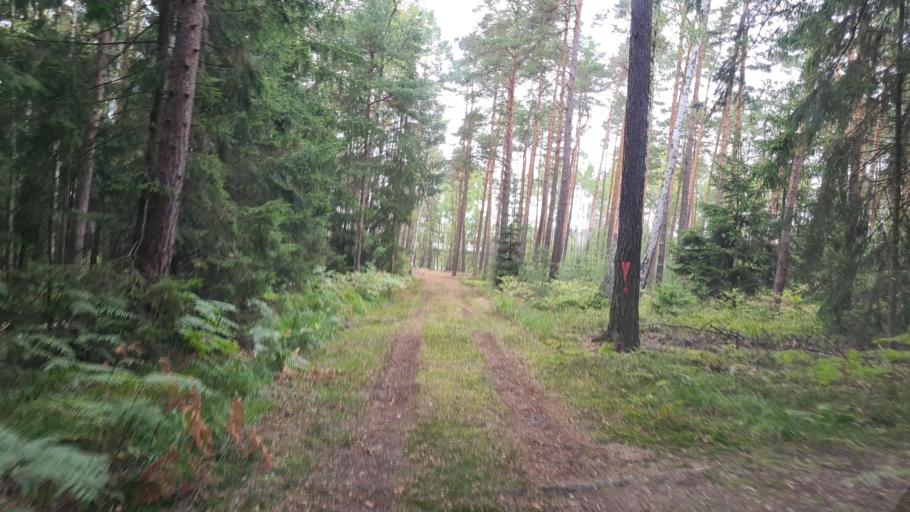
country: DE
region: Brandenburg
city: Schonborn
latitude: 51.6257
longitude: 13.5183
